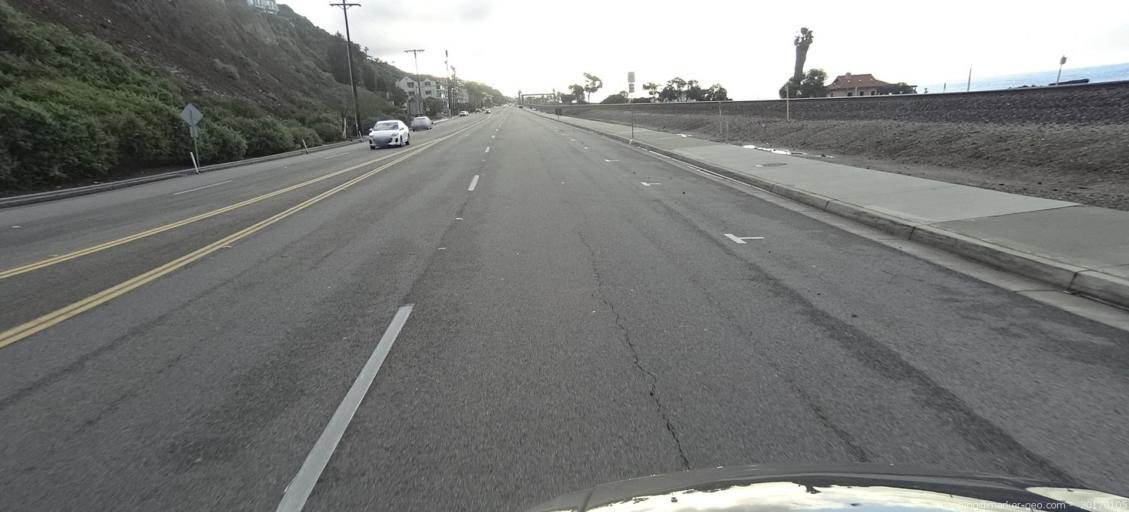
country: US
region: California
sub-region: Orange County
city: Dana Point
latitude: 33.4619
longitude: -117.6783
